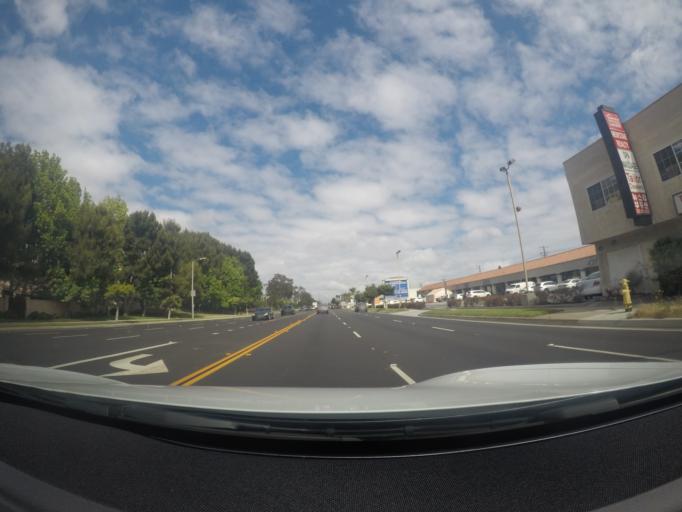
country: US
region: California
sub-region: Los Angeles County
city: Torrance
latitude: 33.8230
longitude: -118.3343
